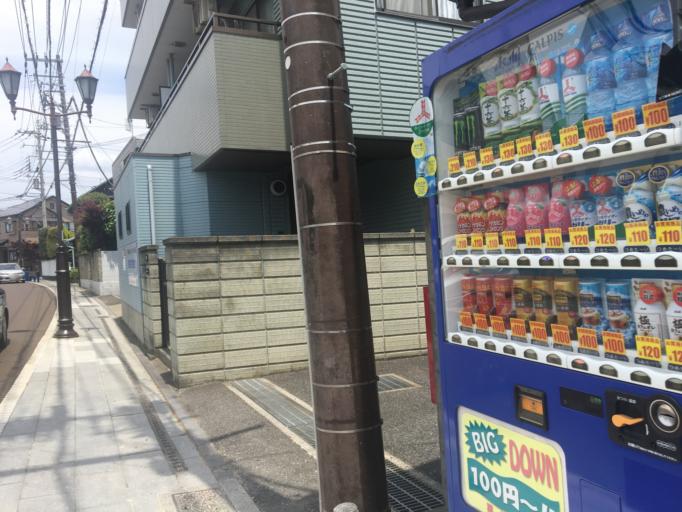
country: JP
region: Saitama
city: Shimotoda
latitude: 35.8212
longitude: 139.6814
